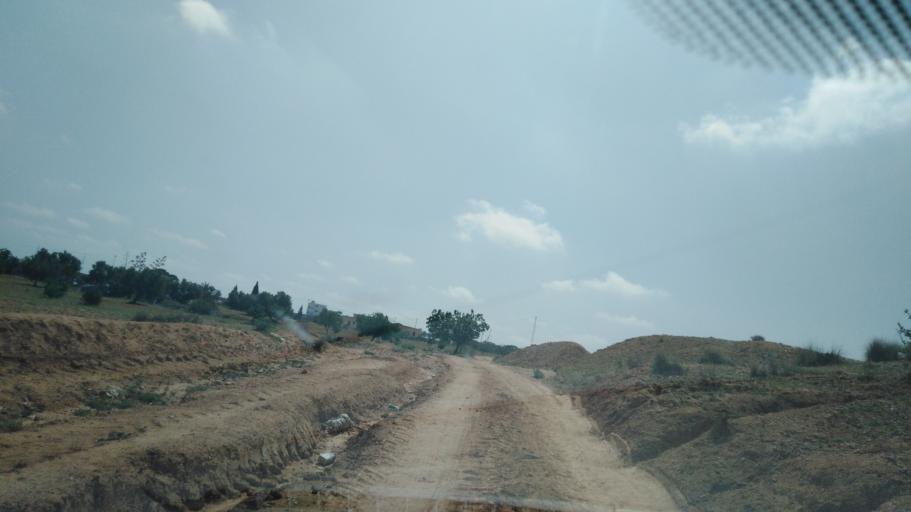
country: TN
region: Safaqis
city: Sfax
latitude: 34.7269
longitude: 10.5707
